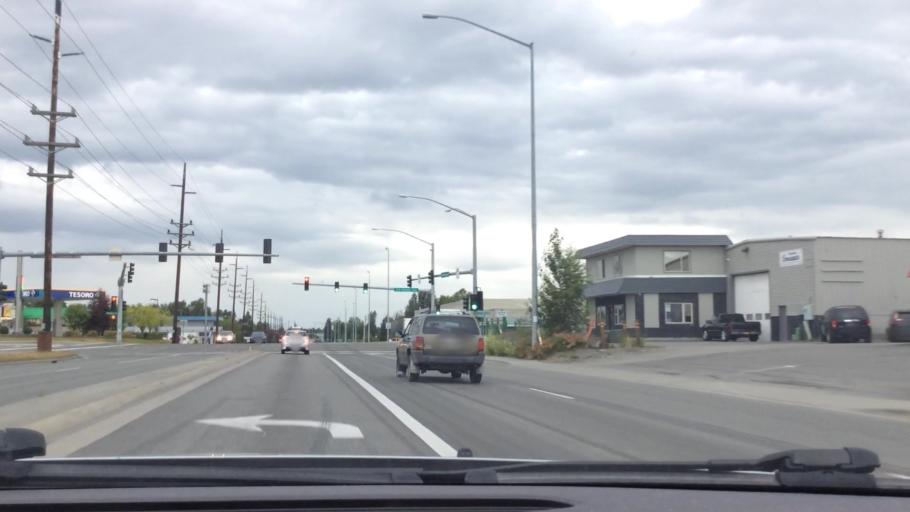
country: US
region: Alaska
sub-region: Anchorage Municipality
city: Anchorage
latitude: 61.1664
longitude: -149.8662
